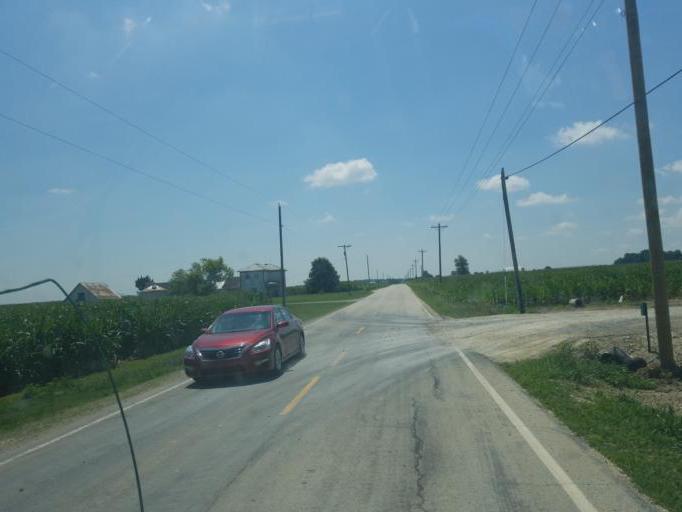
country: US
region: Ohio
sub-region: Allen County
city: Spencerville
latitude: 40.6905
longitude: -84.4256
